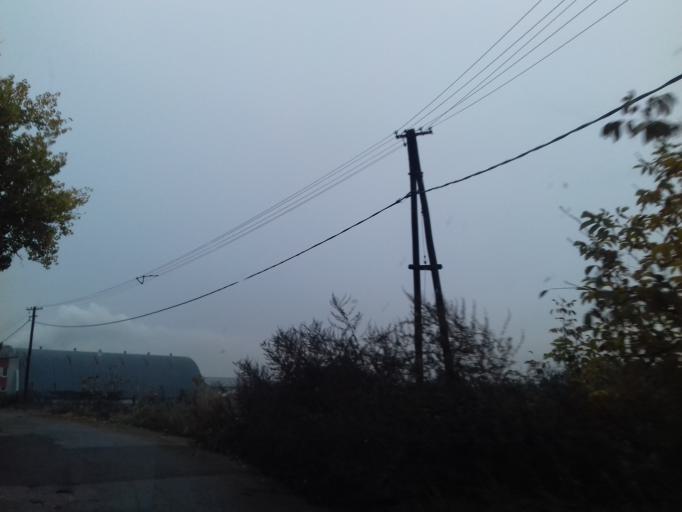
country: SK
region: Bratislavsky
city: Bratislava
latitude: 48.1378
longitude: 17.1714
